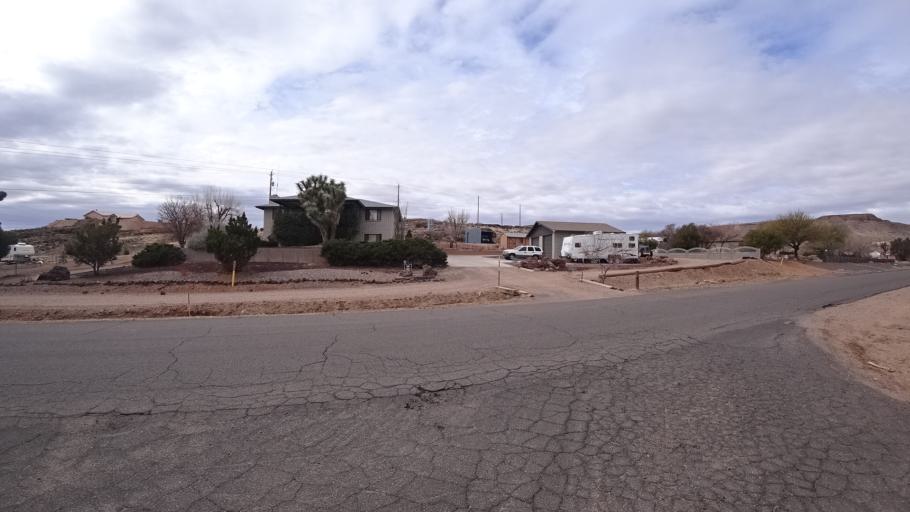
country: US
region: Arizona
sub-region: Mohave County
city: New Kingman-Butler
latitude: 35.2299
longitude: -114.0452
